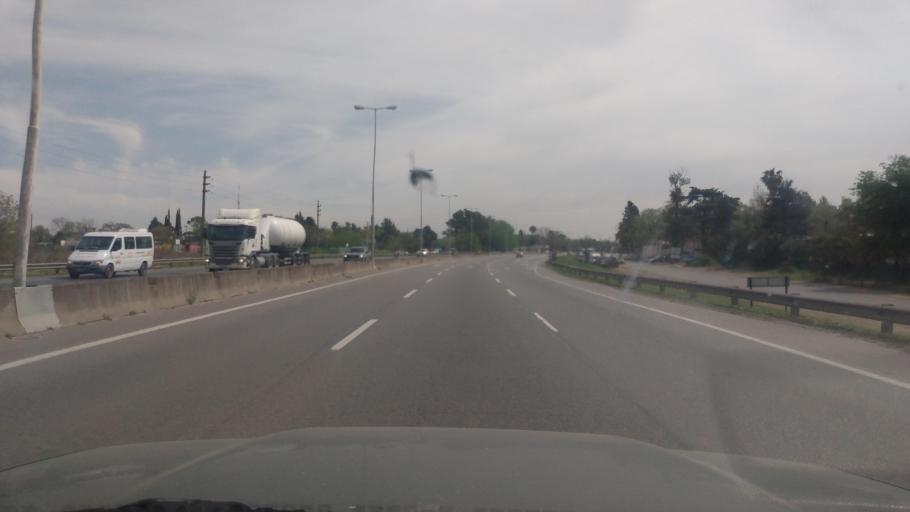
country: AR
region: Buenos Aires
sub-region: Partido de Pilar
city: Pilar
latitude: -34.4367
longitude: -58.9852
